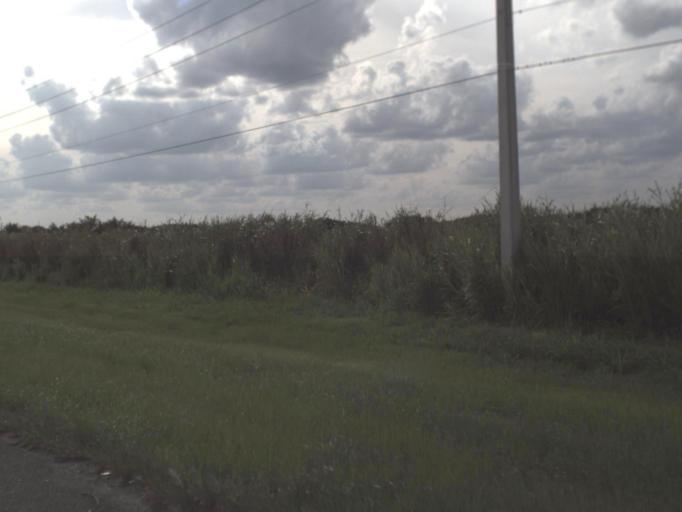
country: US
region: Florida
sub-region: Hendry County
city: LaBelle
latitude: 26.7124
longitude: -81.5057
